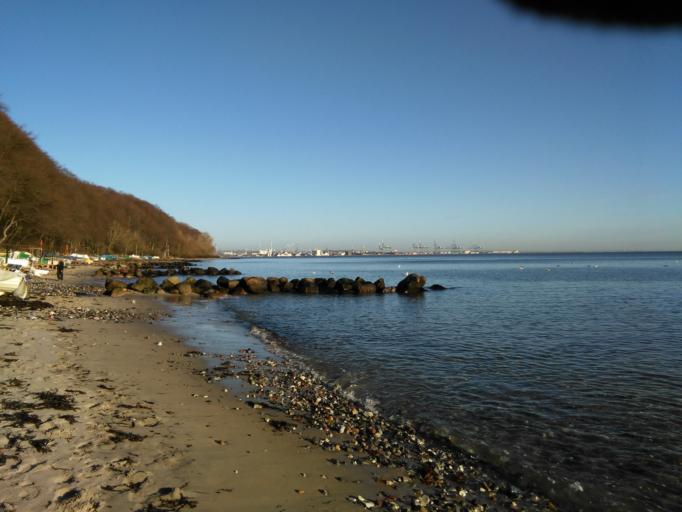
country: DK
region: Central Jutland
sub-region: Arhus Kommune
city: Arhus
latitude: 56.1145
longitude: 10.2302
